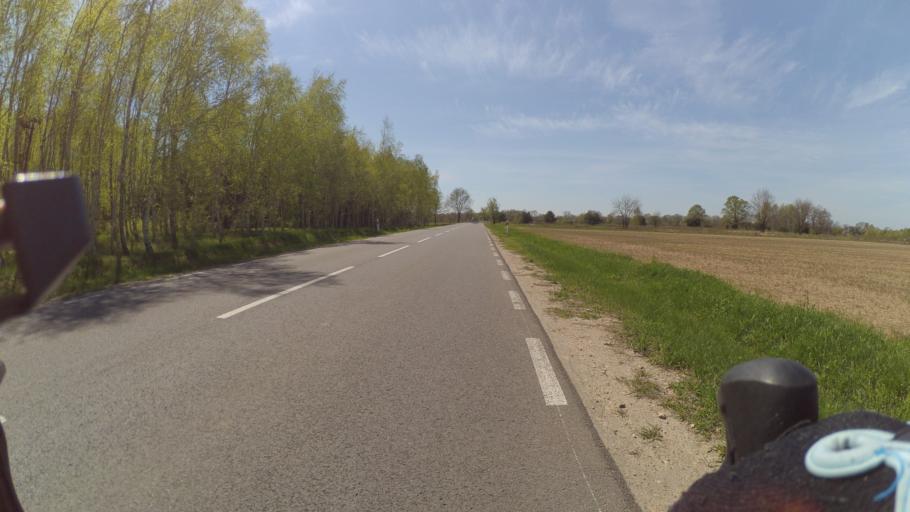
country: PL
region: Masovian Voivodeship
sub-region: Powiat plonski
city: Czerwinsk Nad Wisla
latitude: 52.3767
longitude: 20.3141
